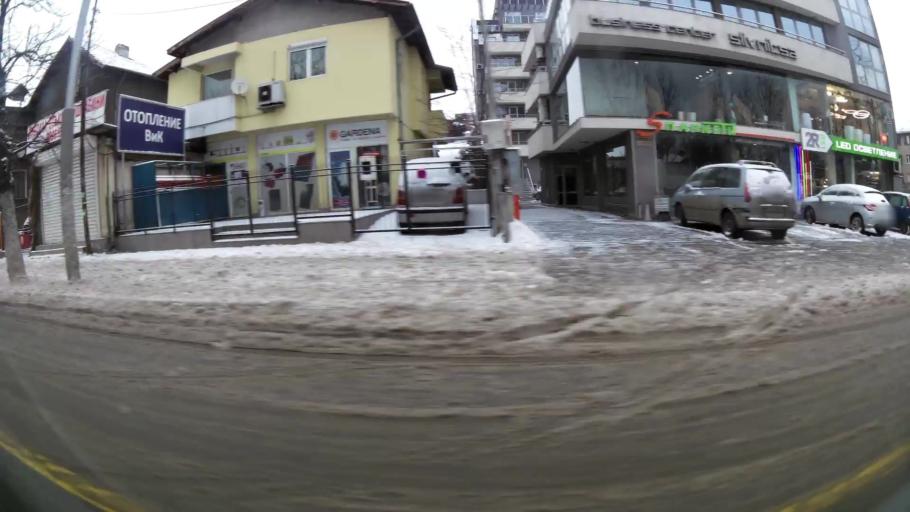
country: BG
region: Sofia-Capital
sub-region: Stolichna Obshtina
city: Sofia
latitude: 42.7063
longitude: 23.3096
